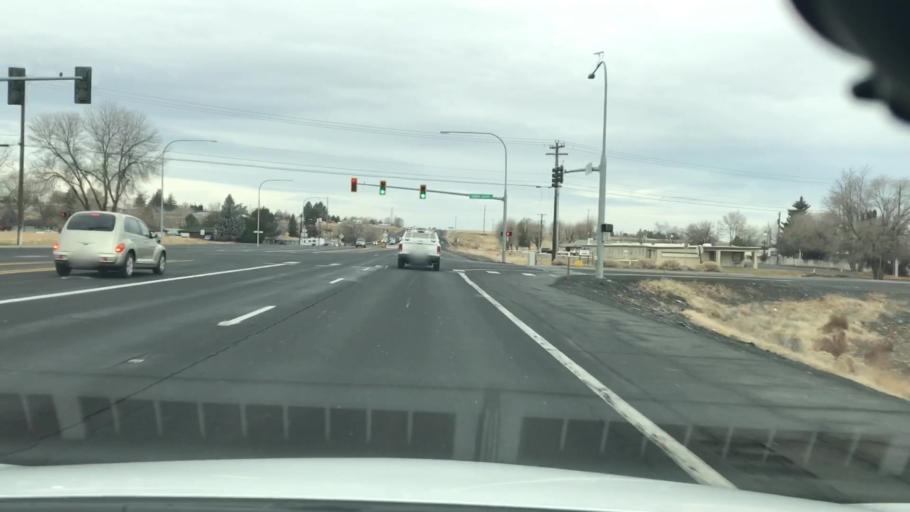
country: US
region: Washington
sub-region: Grant County
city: Moses Lake
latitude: 47.1494
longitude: -119.2934
